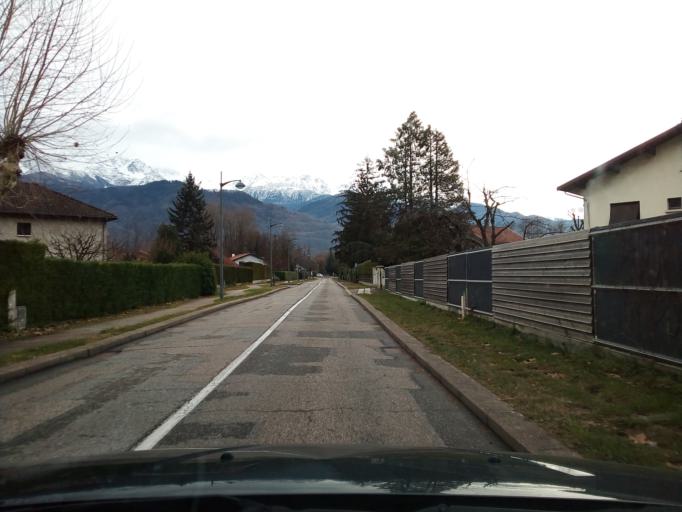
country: FR
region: Rhone-Alpes
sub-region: Departement de l'Isere
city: Crolles
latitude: 45.2751
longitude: 5.8923
